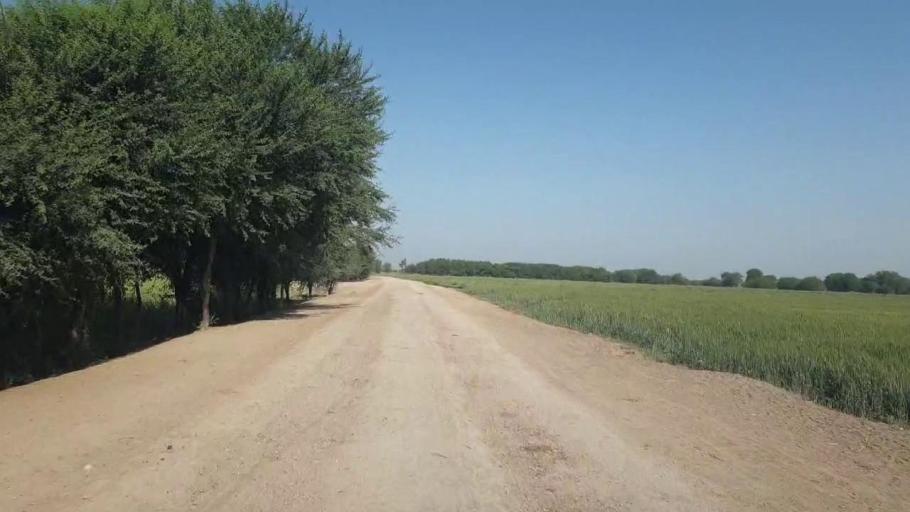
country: PK
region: Sindh
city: Umarkot
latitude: 25.3005
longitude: 69.6543
